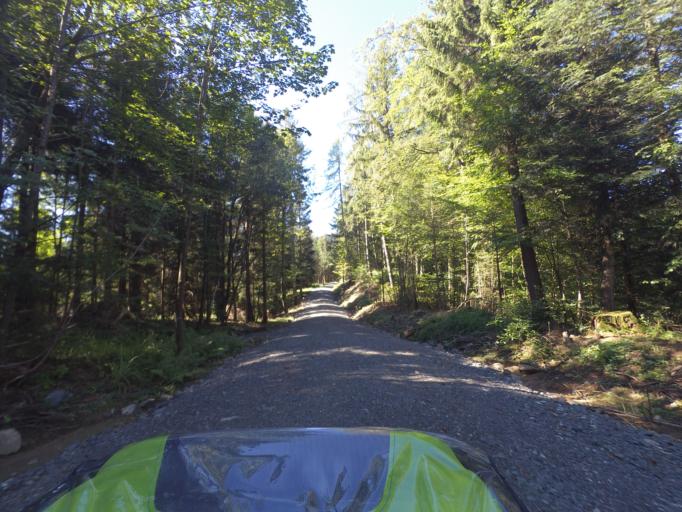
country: AT
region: Salzburg
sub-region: Politischer Bezirk Hallein
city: Hallein
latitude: 47.6548
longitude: 13.1025
